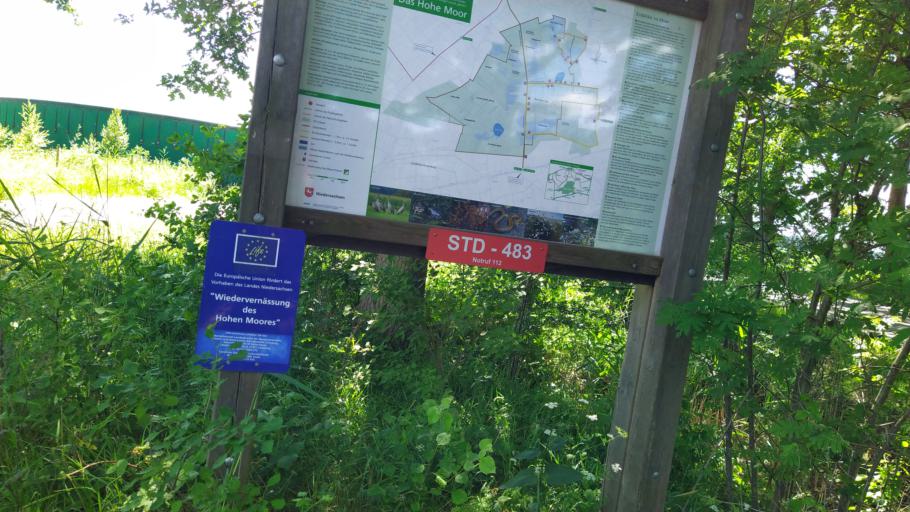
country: DE
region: Lower Saxony
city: Oldendorf
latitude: 53.5679
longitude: 9.2467
